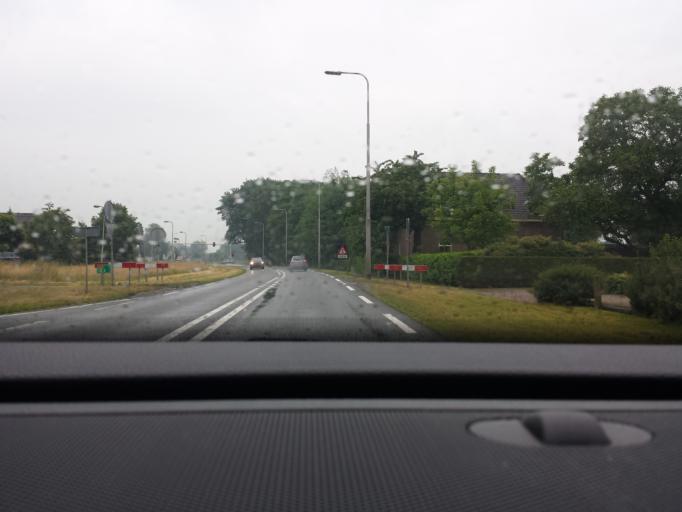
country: NL
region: Overijssel
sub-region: Gemeente Haaksbergen
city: Haaksbergen
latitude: 52.1499
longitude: 6.7407
